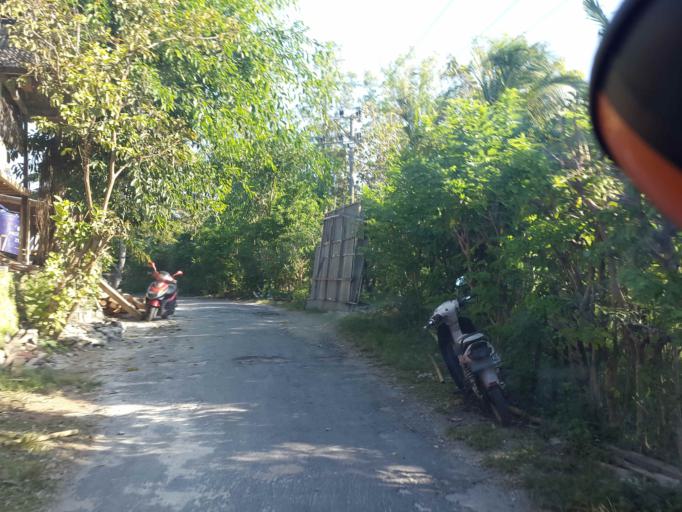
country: ID
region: Bali
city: Gelagah
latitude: -8.7081
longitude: 115.5600
